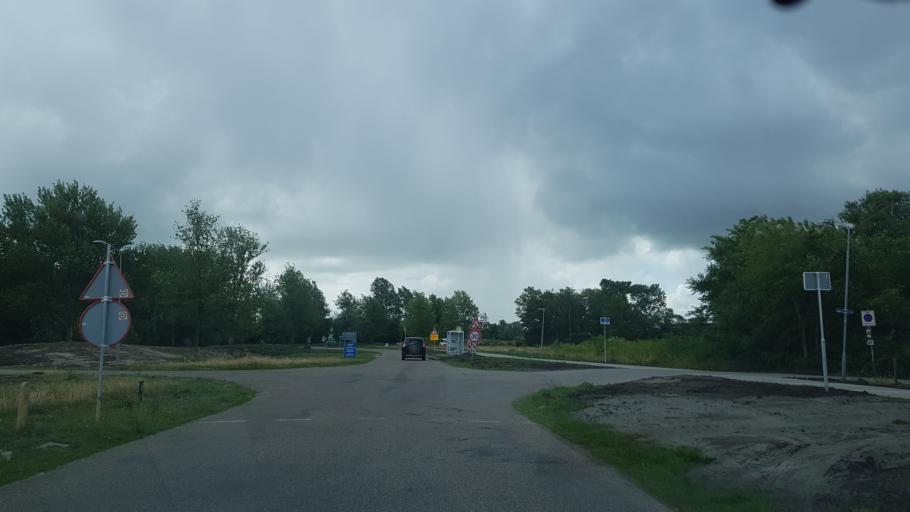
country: NL
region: Friesland
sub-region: Gemeente Dongeradeel
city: Anjum
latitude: 53.4057
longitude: 6.2120
